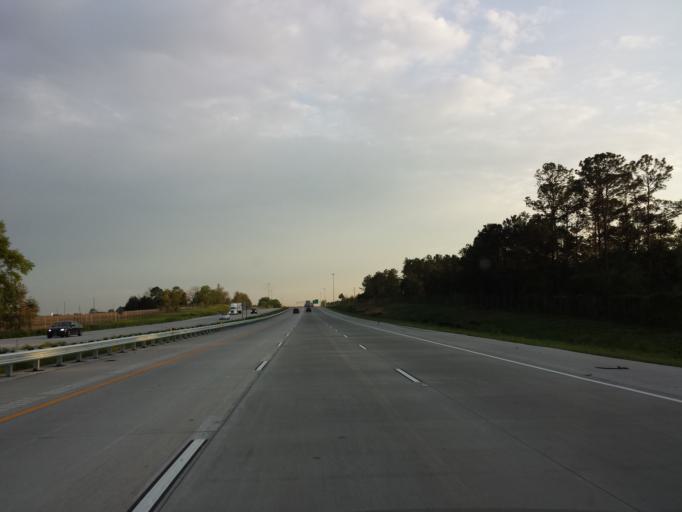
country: US
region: Georgia
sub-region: Dooly County
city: Vienna
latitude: 32.1308
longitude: -83.7597
